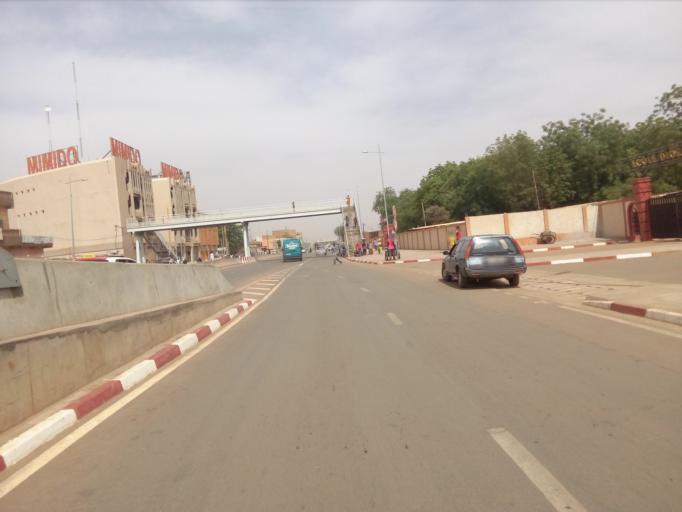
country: NE
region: Niamey
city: Niamey
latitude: 13.5215
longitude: 2.1176
